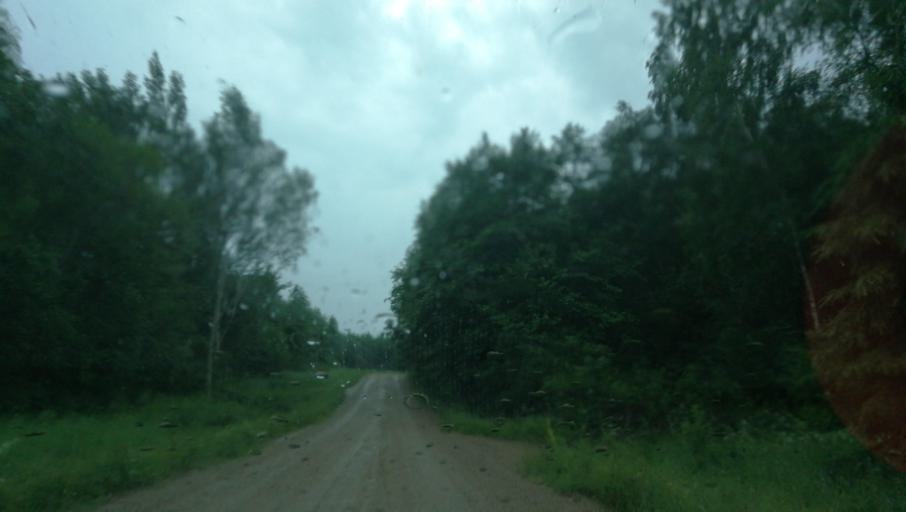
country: LV
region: Vecpiebalga
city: Vecpiebalga
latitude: 57.1044
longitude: 25.6919
